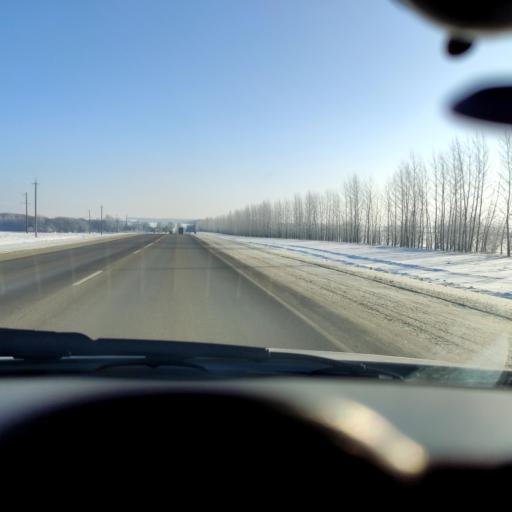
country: RU
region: Kursk
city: Tim
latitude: 51.6534
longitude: 36.9414
